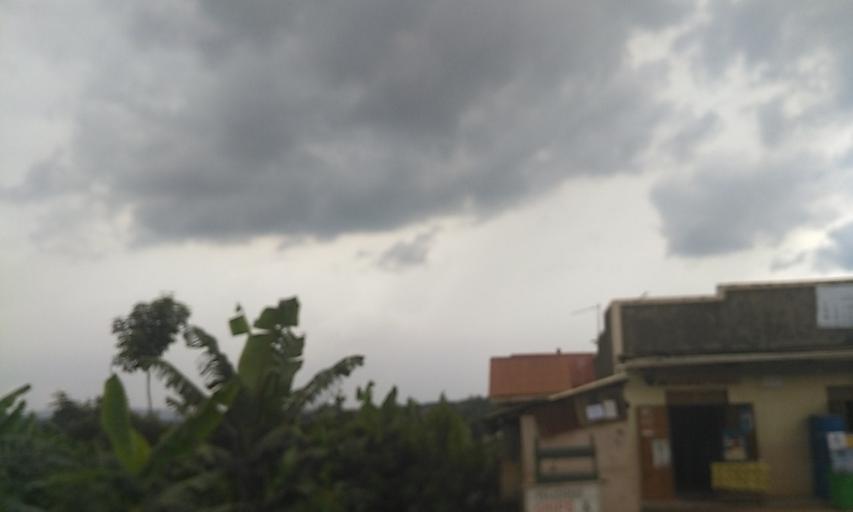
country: UG
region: Central Region
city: Kampala Central Division
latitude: 0.3267
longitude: 32.4980
